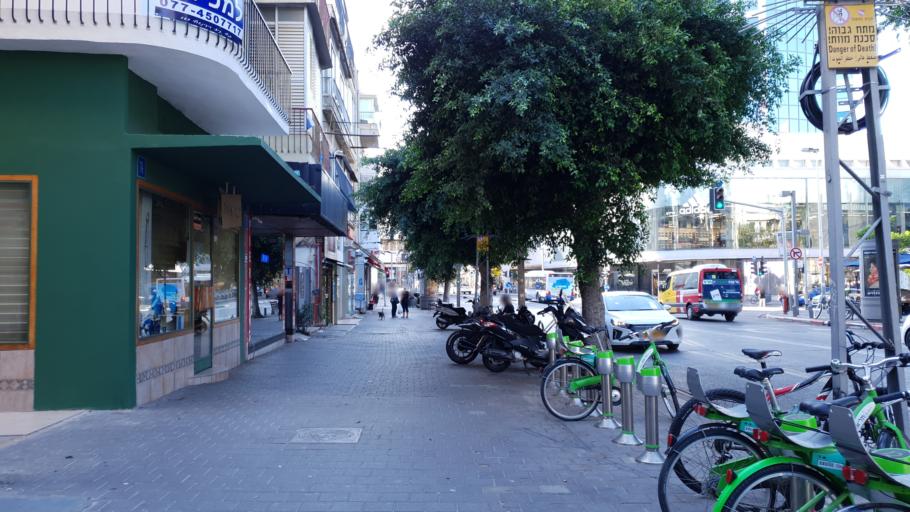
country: IL
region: Tel Aviv
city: Tel Aviv
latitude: 32.0765
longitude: 34.7747
